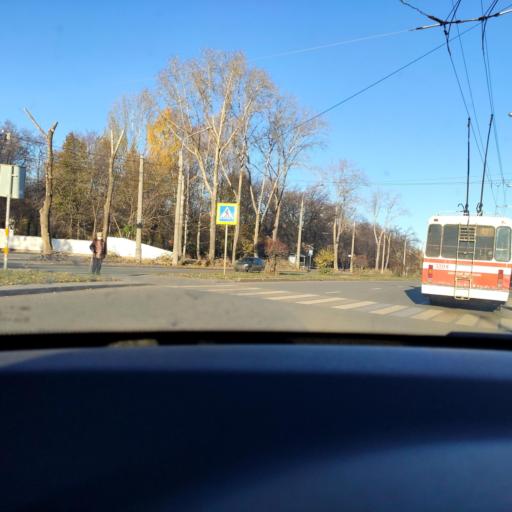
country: RU
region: Samara
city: Samara
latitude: 53.2293
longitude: 50.2068
